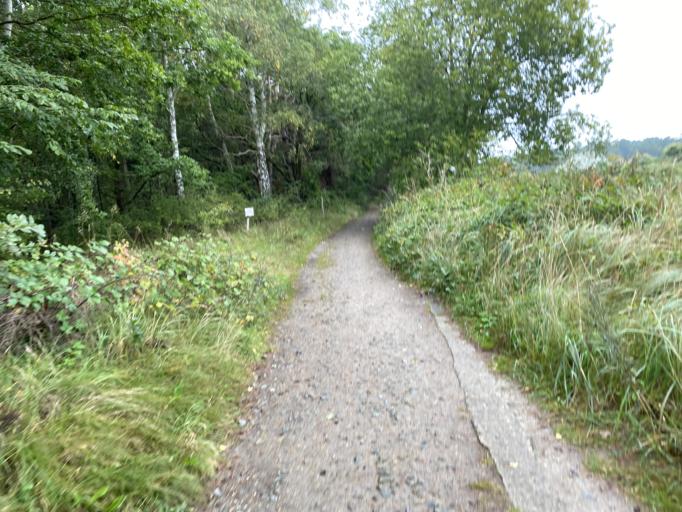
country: DE
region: Mecklenburg-Vorpommern
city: Ostseebad Binz
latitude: 54.4406
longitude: 13.5608
